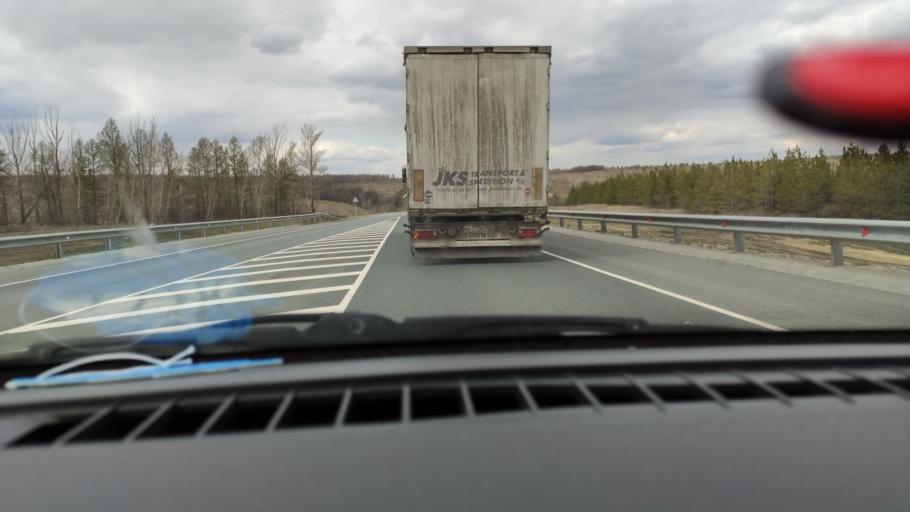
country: RU
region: Saratov
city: Shikhany
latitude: 52.1397
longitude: 47.2102
